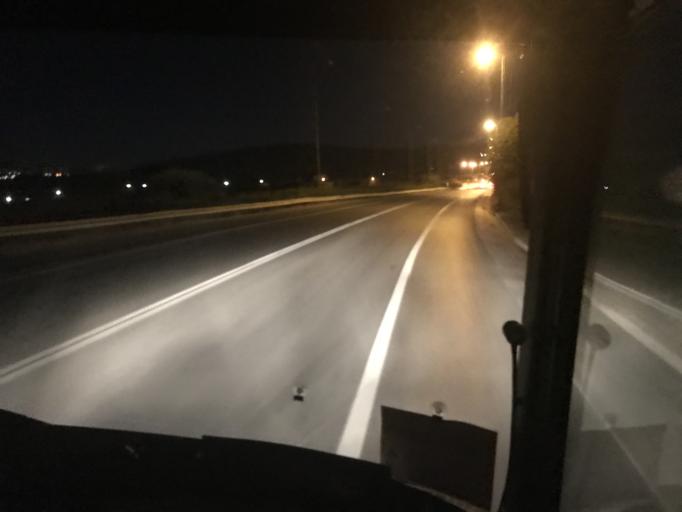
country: GR
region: Crete
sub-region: Nomos Irakleiou
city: Skalanion
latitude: 35.2793
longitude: 25.1806
